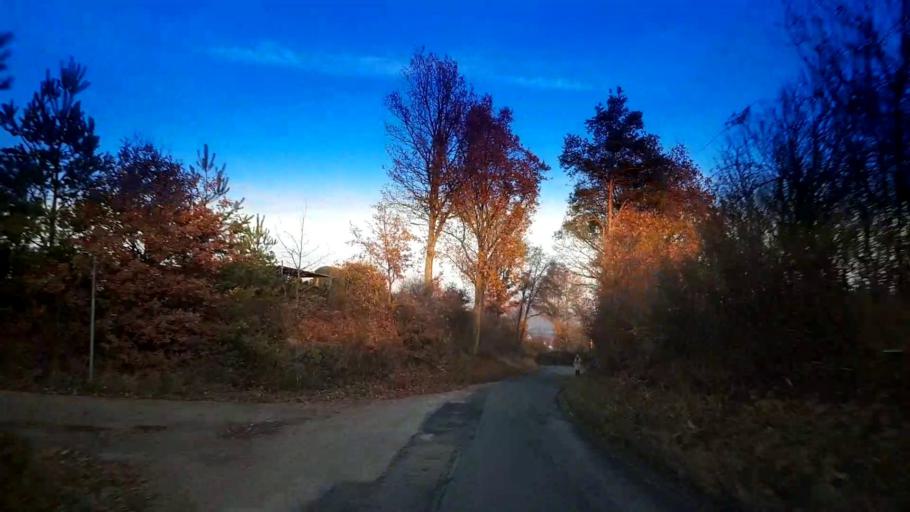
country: DE
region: Bavaria
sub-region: Upper Franconia
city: Walsdorf
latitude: 49.8646
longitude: 10.8067
